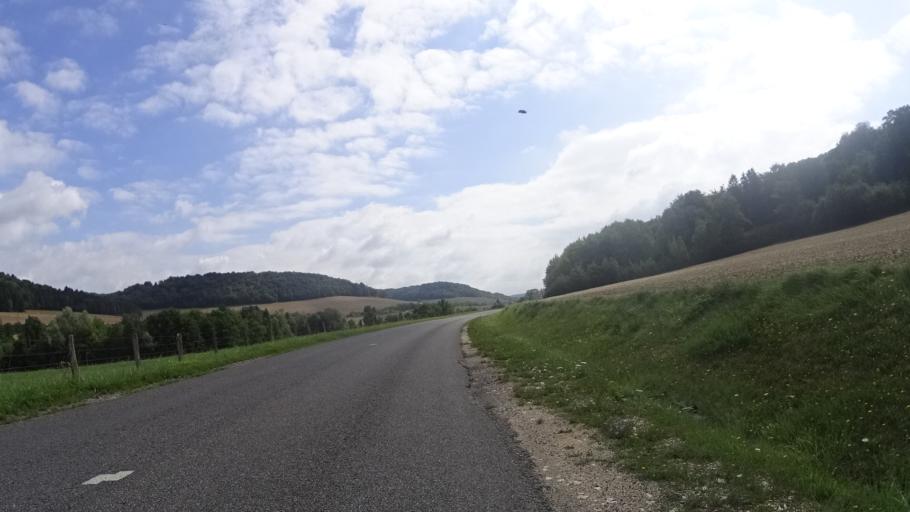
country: FR
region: Lorraine
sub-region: Departement de la Meuse
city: Ligny-en-Barrois
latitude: 48.7189
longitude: 5.3338
